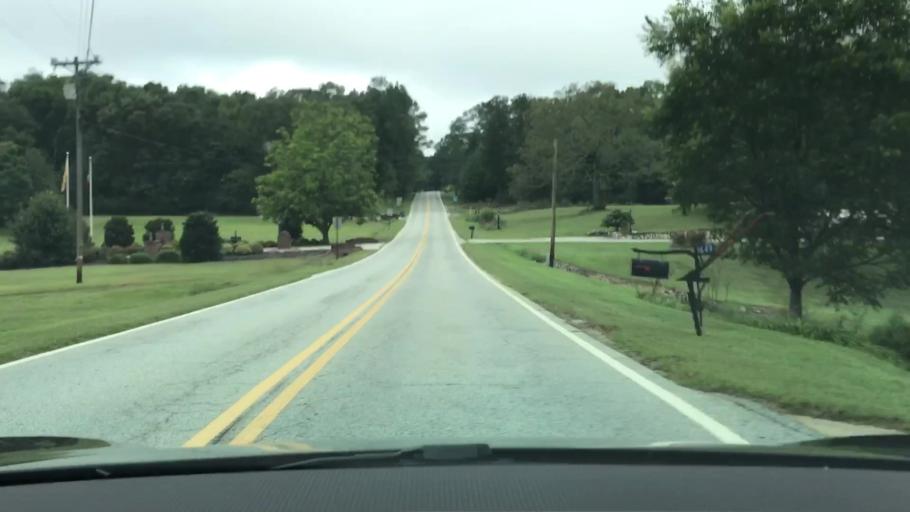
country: US
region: Georgia
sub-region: Barrow County
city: Auburn
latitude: 34.0689
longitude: -83.8401
